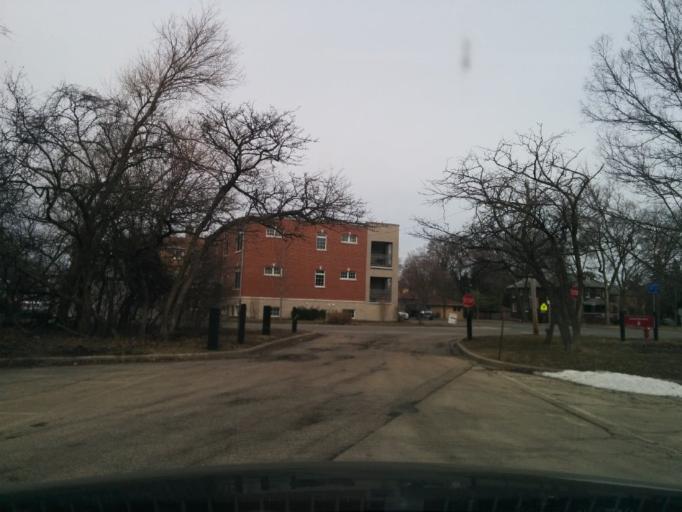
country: US
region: Illinois
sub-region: Cook County
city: North Riverside
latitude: 41.8406
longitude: -87.8234
